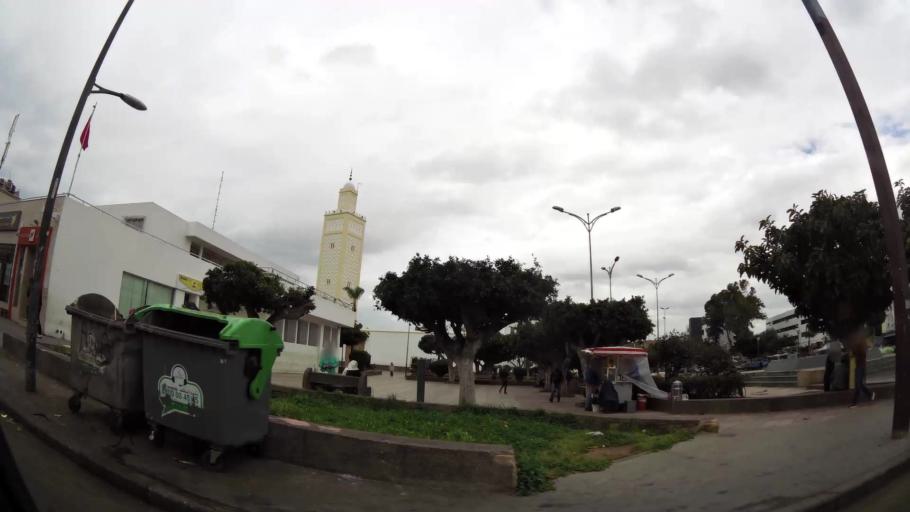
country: MA
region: Grand Casablanca
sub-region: Casablanca
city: Casablanca
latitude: 33.5861
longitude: -7.5668
